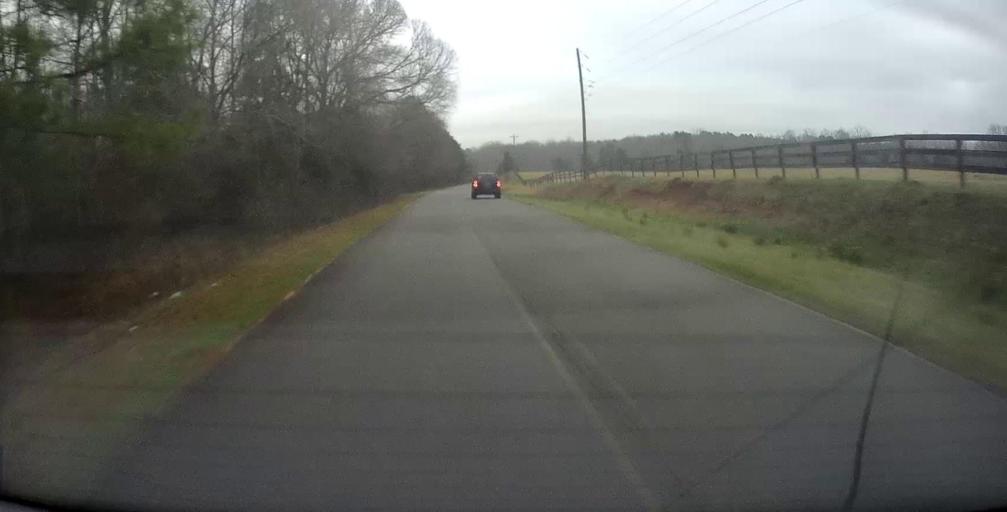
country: US
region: Georgia
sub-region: Lamar County
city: Barnesville
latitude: 33.0258
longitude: -84.1126
